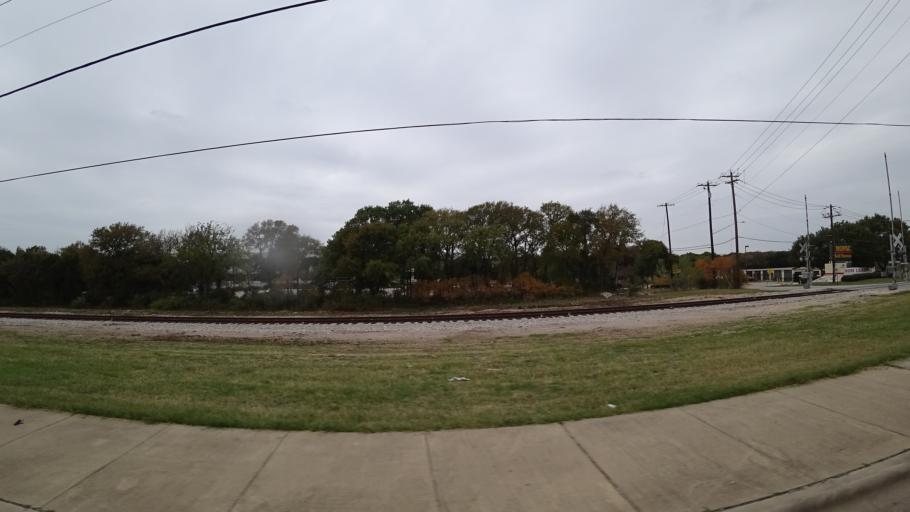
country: US
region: Texas
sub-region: Travis County
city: Wells Branch
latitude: 30.4260
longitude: -97.7029
